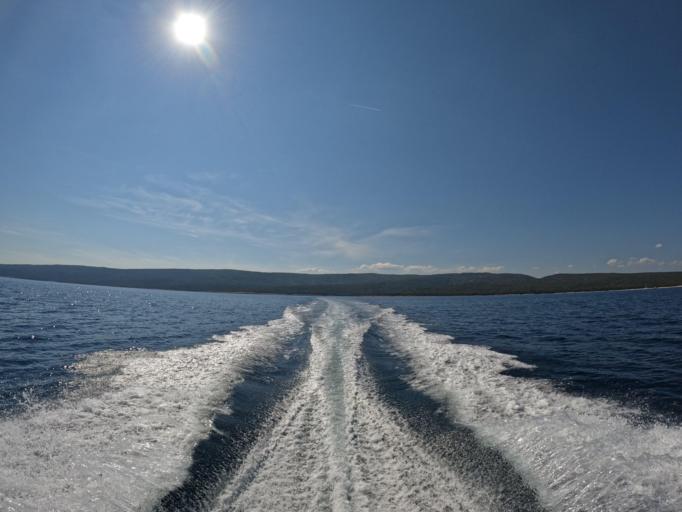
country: HR
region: Primorsko-Goranska
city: Cres
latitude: 44.9454
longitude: 14.4887
